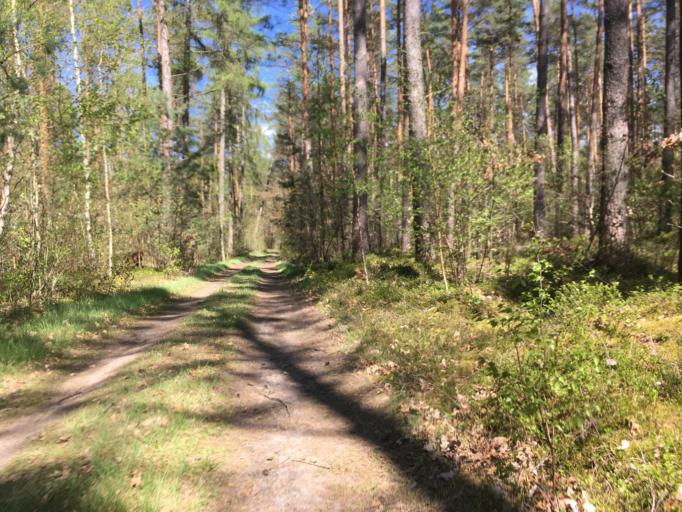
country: DE
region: Brandenburg
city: Wandlitz
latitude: 52.7083
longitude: 13.5033
